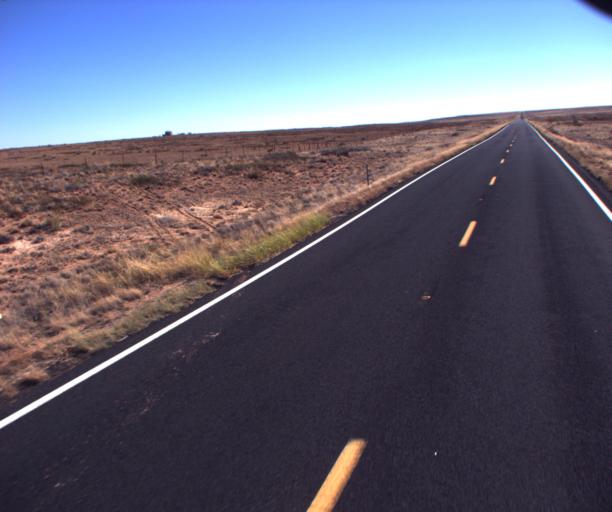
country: US
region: Arizona
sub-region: Coconino County
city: Tuba City
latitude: 35.9916
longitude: -111.0148
